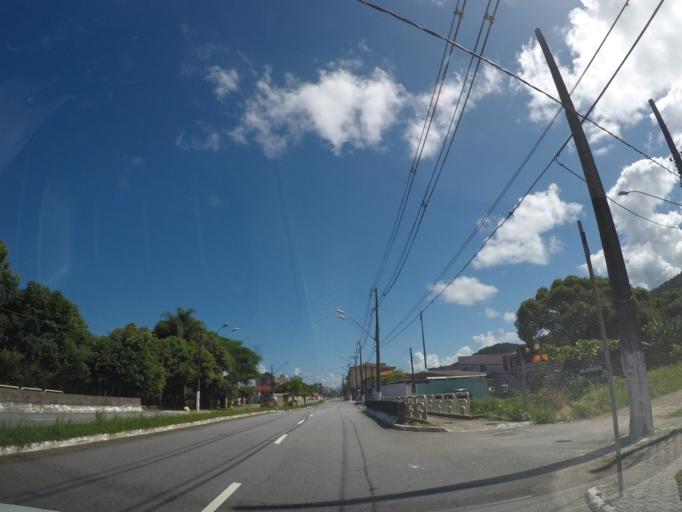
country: BR
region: Sao Paulo
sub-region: Mongagua
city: Mongagua
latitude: -24.0827
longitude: -46.5972
